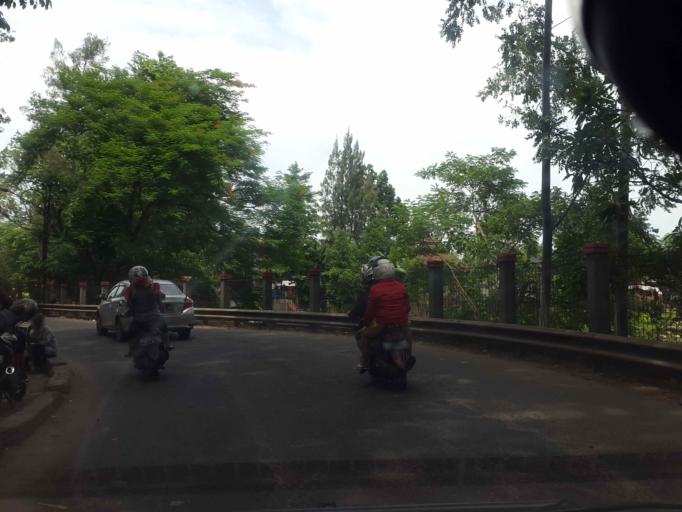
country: ID
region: Banten
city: Tangerang
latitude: -6.1684
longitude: 106.6351
